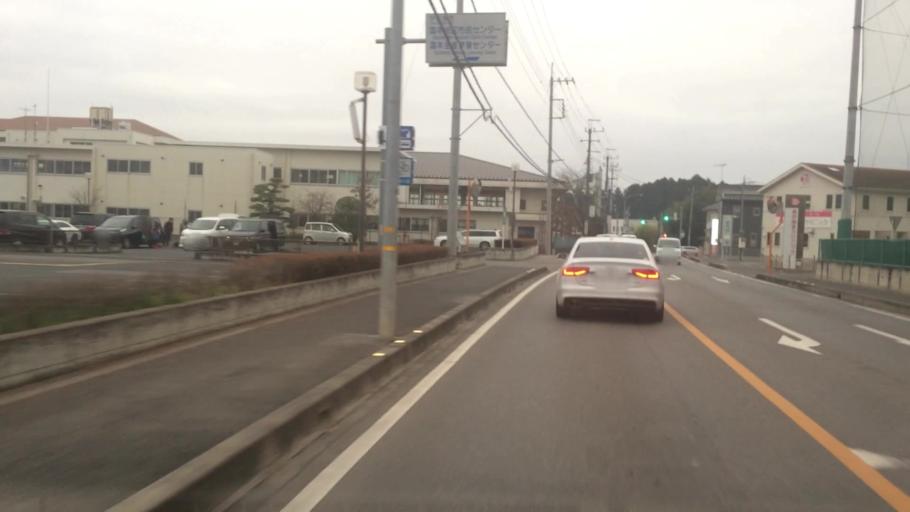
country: JP
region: Tochigi
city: Utsunomiya-shi
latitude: 36.6152
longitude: 139.8390
